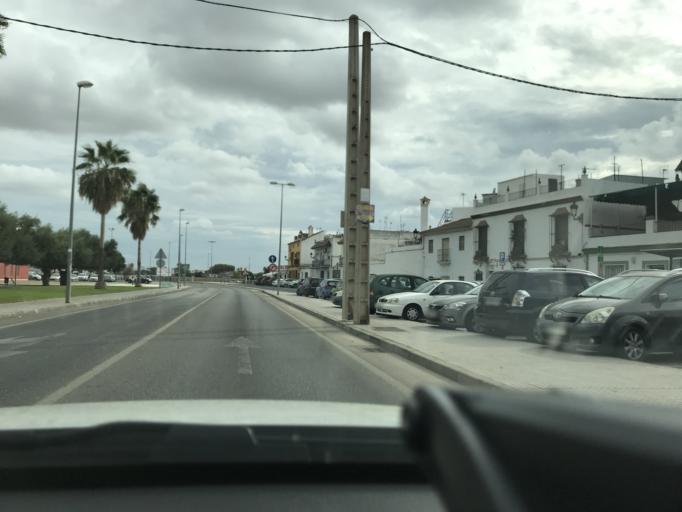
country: ES
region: Andalusia
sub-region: Provincia de Sevilla
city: La Rinconada
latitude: 37.4876
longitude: -5.9779
